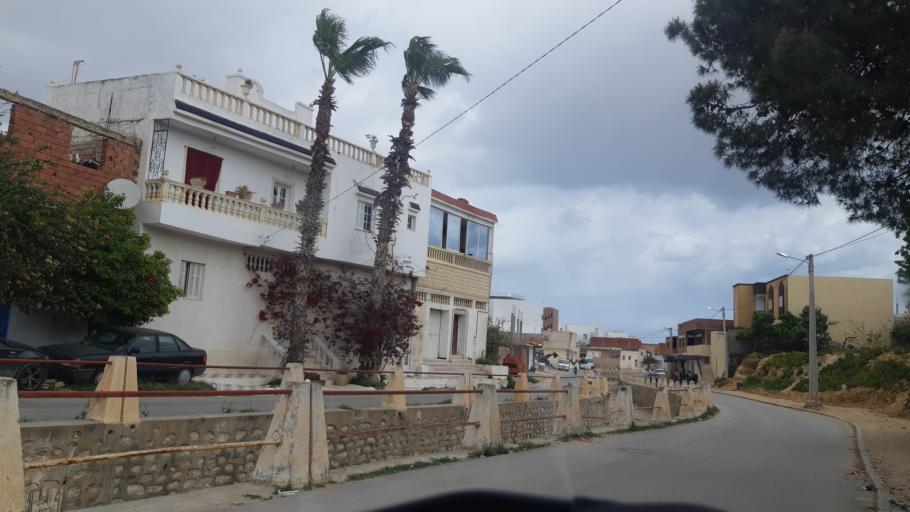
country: TN
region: Susah
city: Akouda
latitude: 35.8673
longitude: 10.5362
